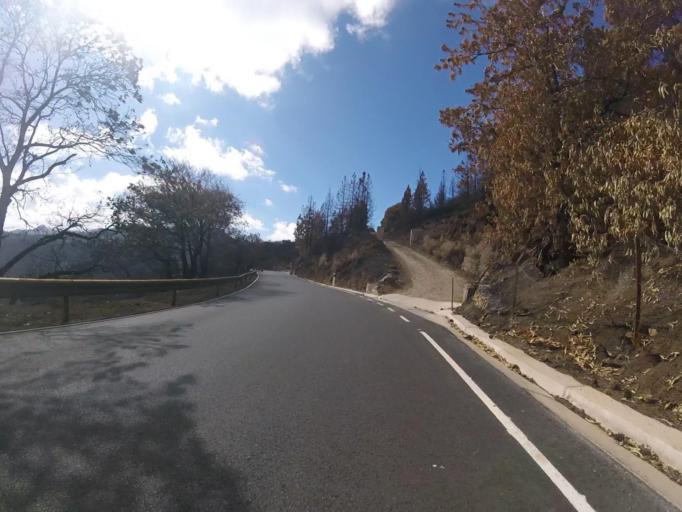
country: ES
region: Canary Islands
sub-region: Provincia de Las Palmas
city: Tejeda
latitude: 27.9975
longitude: -15.5954
